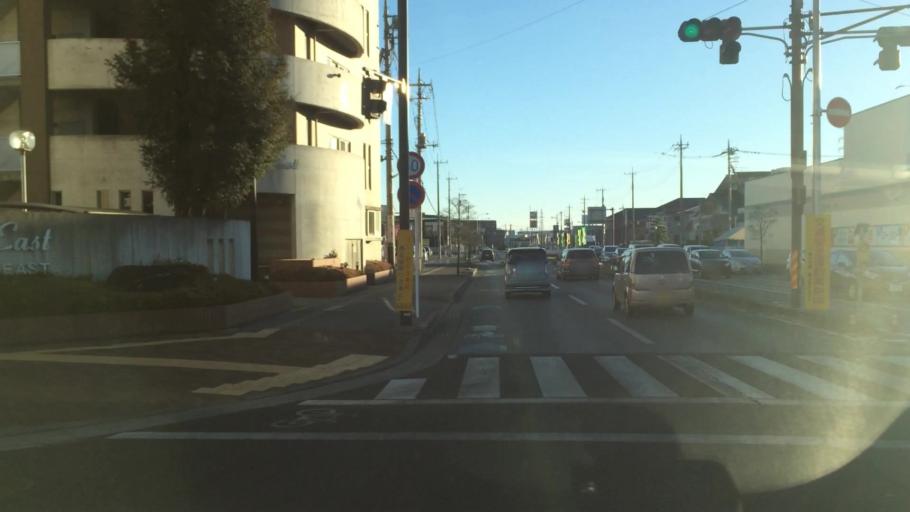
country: JP
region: Tochigi
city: Utsunomiya-shi
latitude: 36.5531
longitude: 139.9026
